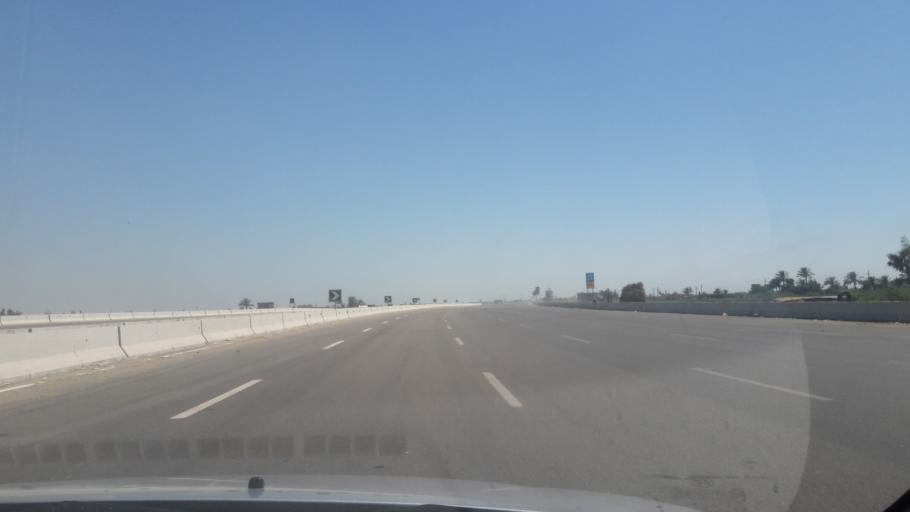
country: EG
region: Muhafazat Bur Sa`id
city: Port Said
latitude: 31.1083
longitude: 32.2339
